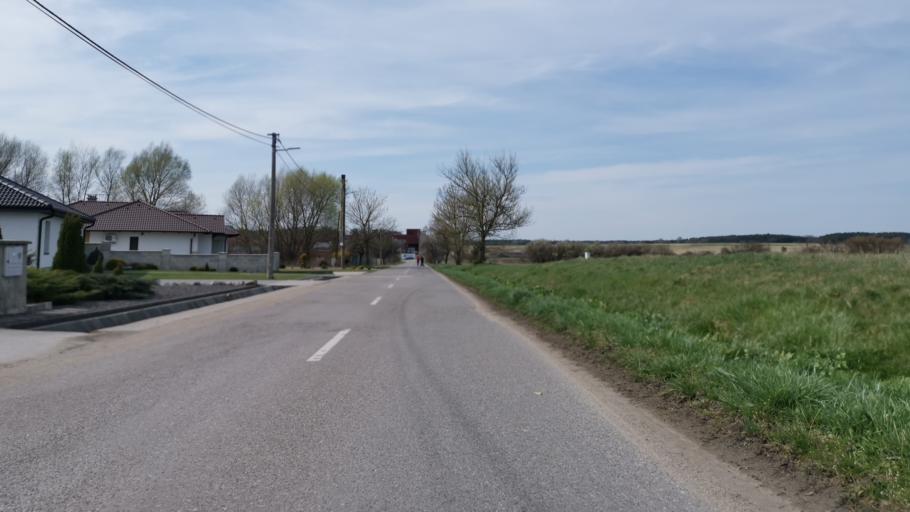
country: SK
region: Trnavsky
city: Gbely
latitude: 48.6582
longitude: 17.0796
